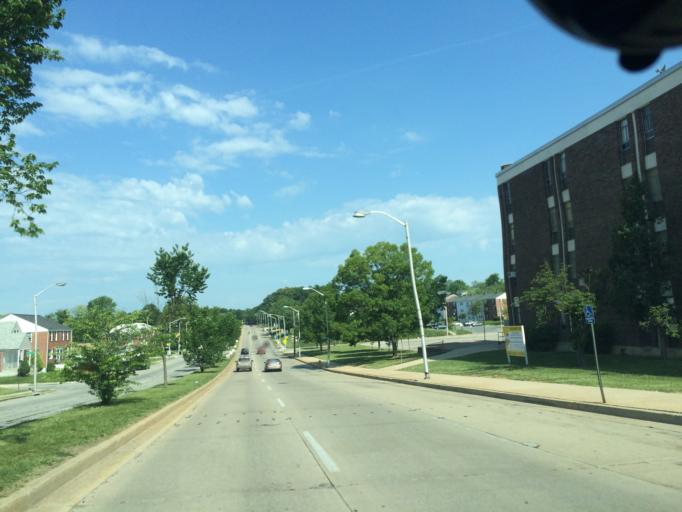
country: US
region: Maryland
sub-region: Baltimore County
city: Parkville
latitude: 39.3661
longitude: -76.5608
